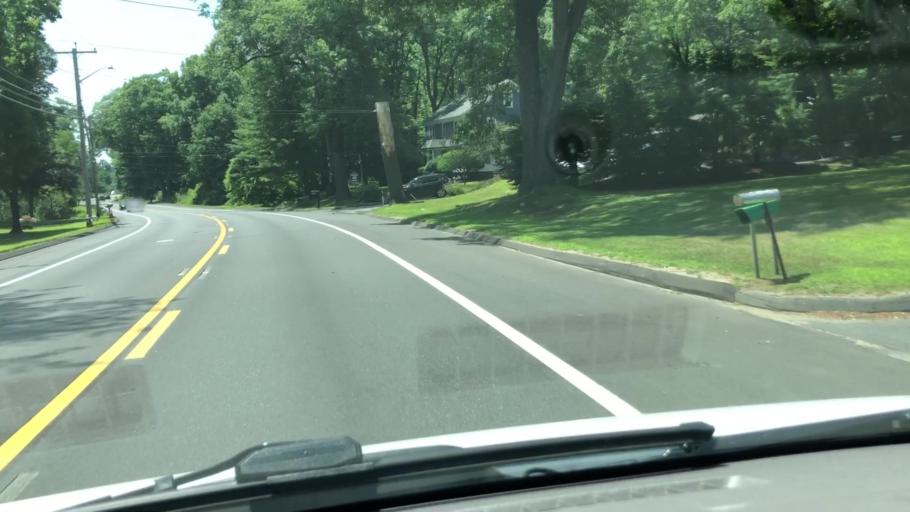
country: US
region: Massachusetts
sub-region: Hampshire County
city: Northampton
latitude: 42.3517
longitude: -72.6424
